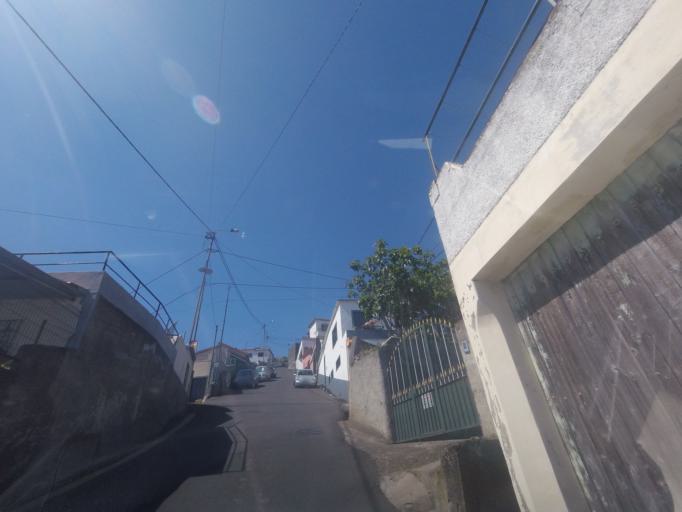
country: PT
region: Madeira
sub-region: Funchal
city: Nossa Senhora do Monte
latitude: 32.6790
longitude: -16.9431
